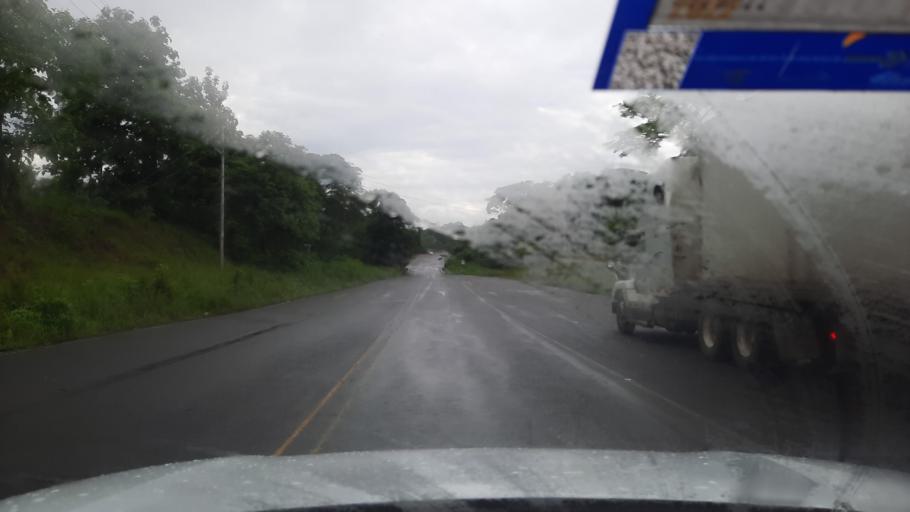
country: NI
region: Rivas
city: Cardenas
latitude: 11.2010
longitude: -85.6187
